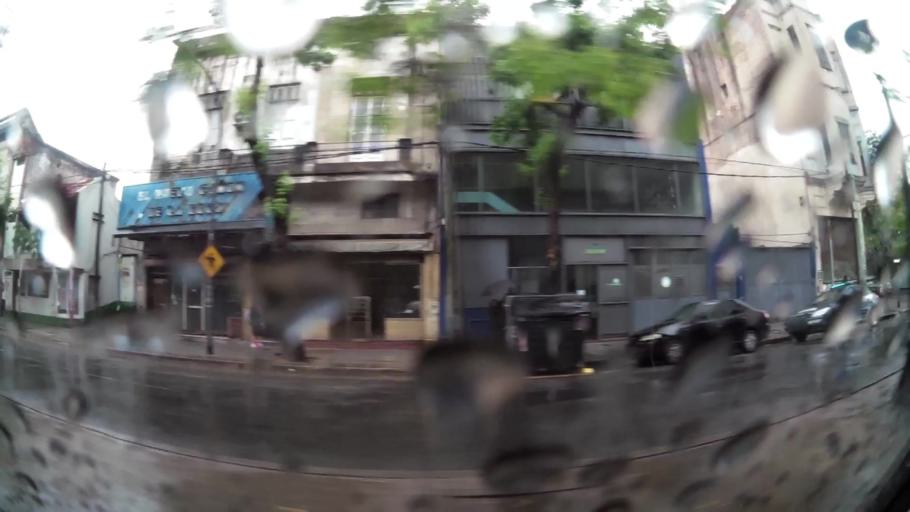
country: AR
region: Buenos Aires
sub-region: Partido de Avellaneda
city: Avellaneda
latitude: -34.6367
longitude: -58.3580
